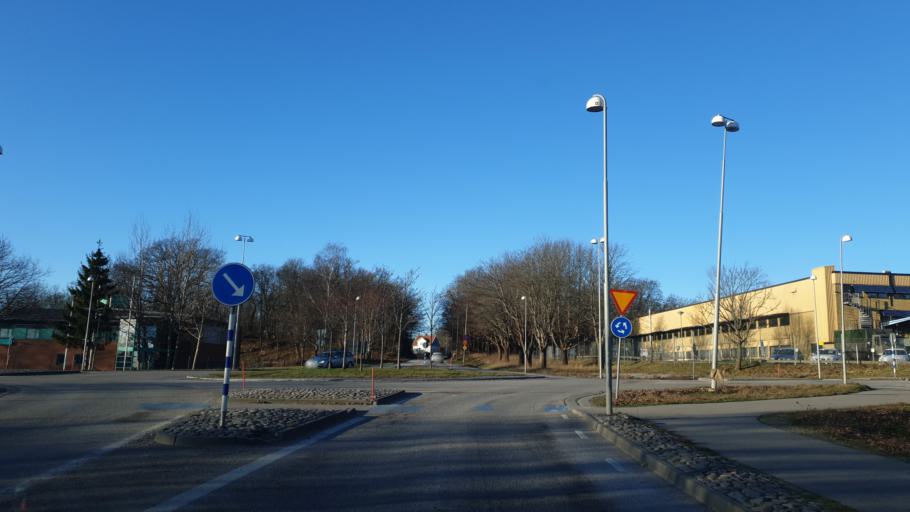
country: SE
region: Blekinge
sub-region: Karlskrona Kommun
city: Rodeby
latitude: 56.2039
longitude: 15.6366
